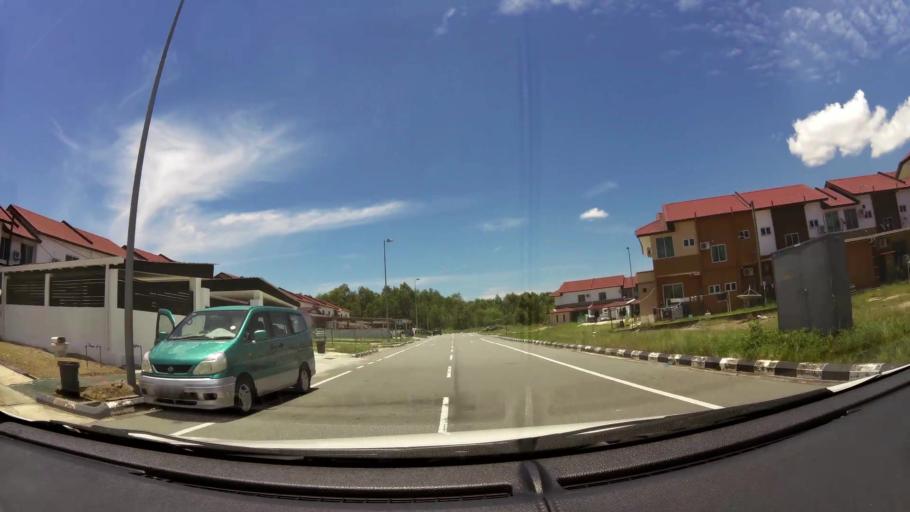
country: BN
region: Brunei and Muara
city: Bandar Seri Begawan
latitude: 5.0127
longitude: 115.0087
